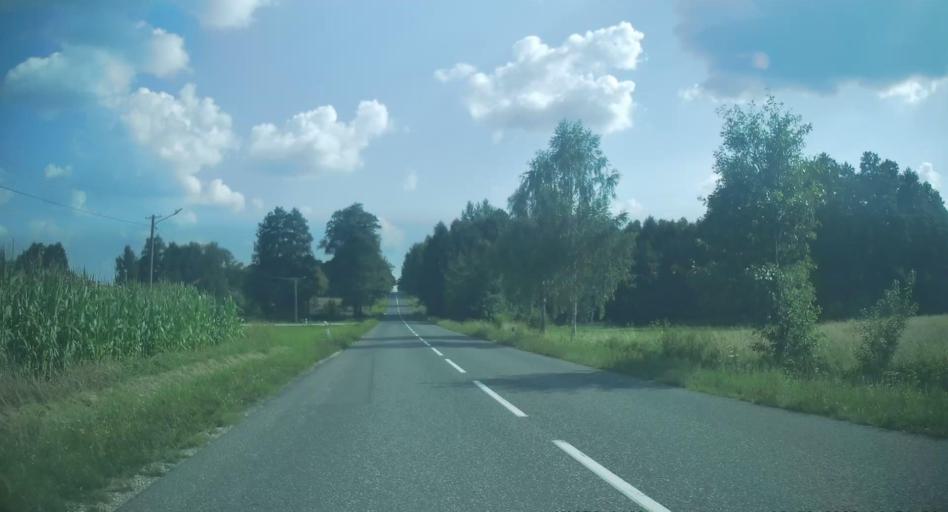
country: PL
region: Swietokrzyskie
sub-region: Powiat kielecki
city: Lopuszno
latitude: 50.9234
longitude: 20.2405
